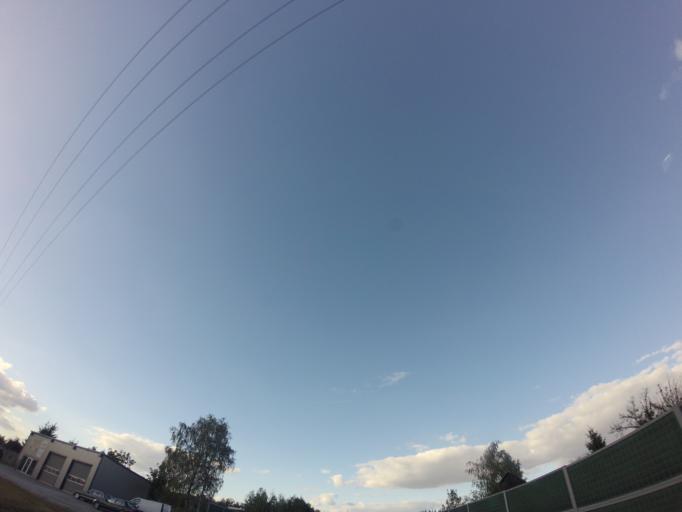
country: PL
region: Greater Poland Voivodeship
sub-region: Powiat nowotomyski
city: Nowy Tomysl
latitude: 52.3156
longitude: 16.1091
